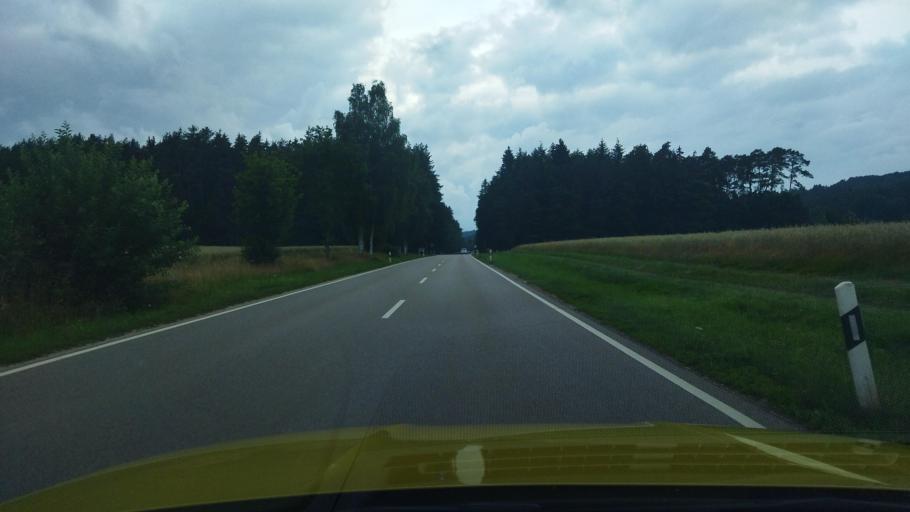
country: DE
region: Bavaria
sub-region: Regierungsbezirk Mittelfranken
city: Pleinfeld
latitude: 49.1040
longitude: 10.9491
